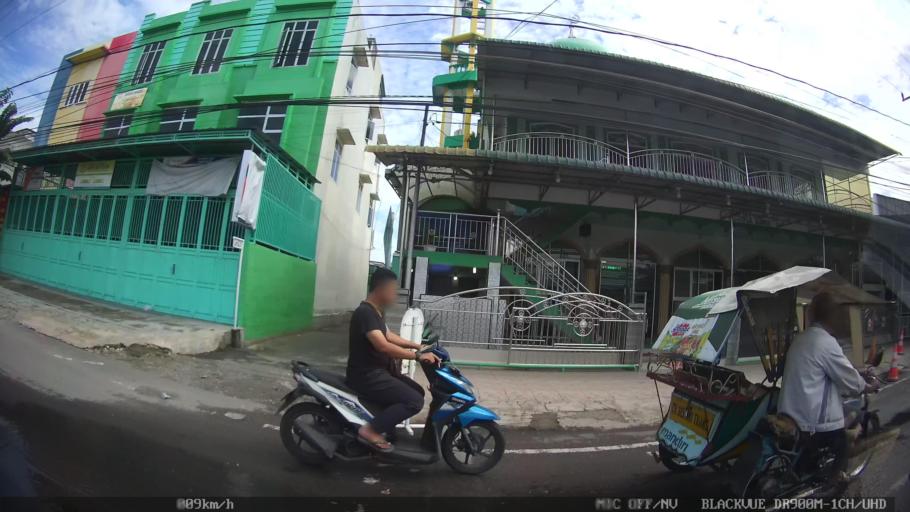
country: ID
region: North Sumatra
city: Medan
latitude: 3.6226
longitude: 98.6875
